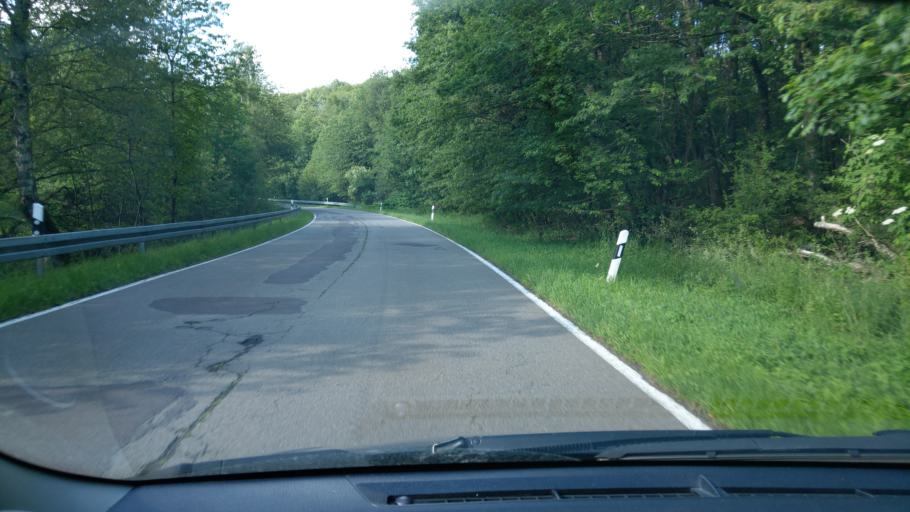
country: DE
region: Saarland
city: Wadern
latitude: 49.5049
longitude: 6.9261
